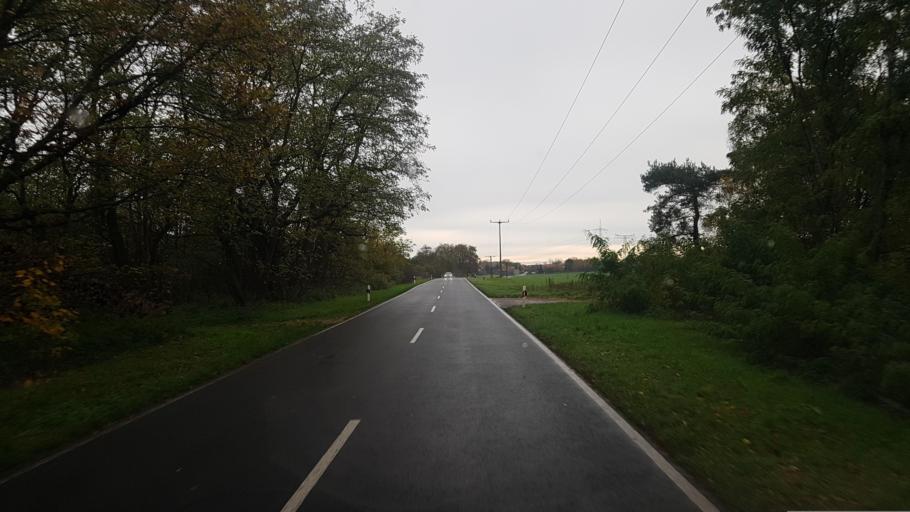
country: DE
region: Saxony-Anhalt
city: Abtsdorf
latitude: 51.8944
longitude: 12.7155
